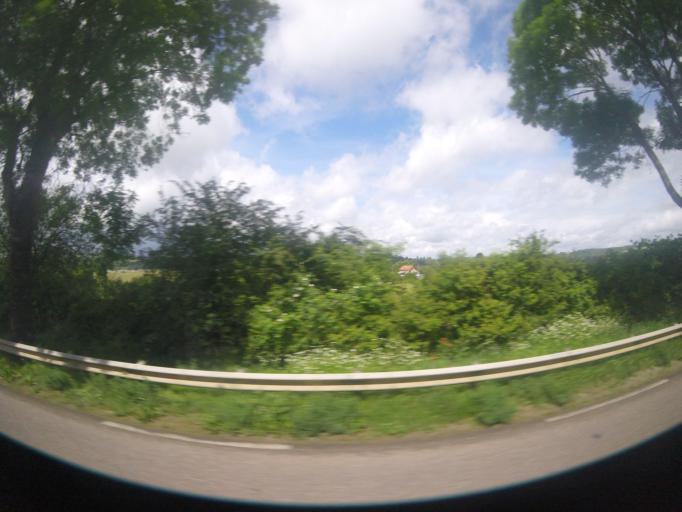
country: FR
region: Lorraine
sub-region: Departement de la Meuse
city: Dugny-sur-Meuse
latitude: 49.1180
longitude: 5.4181
